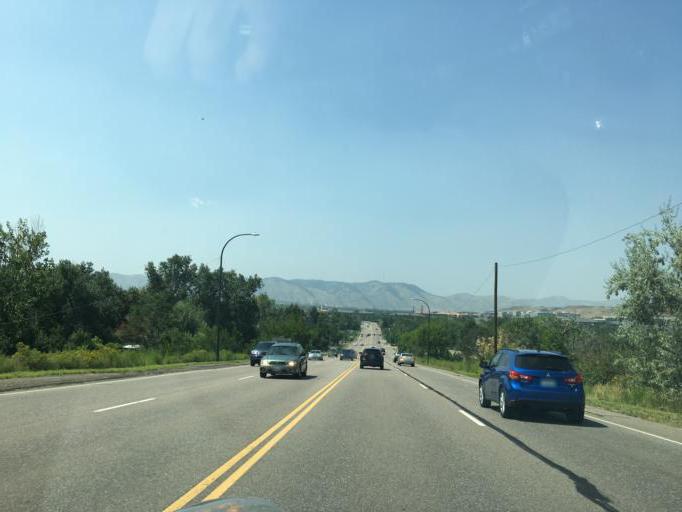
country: US
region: Colorado
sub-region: Jefferson County
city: Applewood
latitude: 39.7396
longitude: -105.1434
